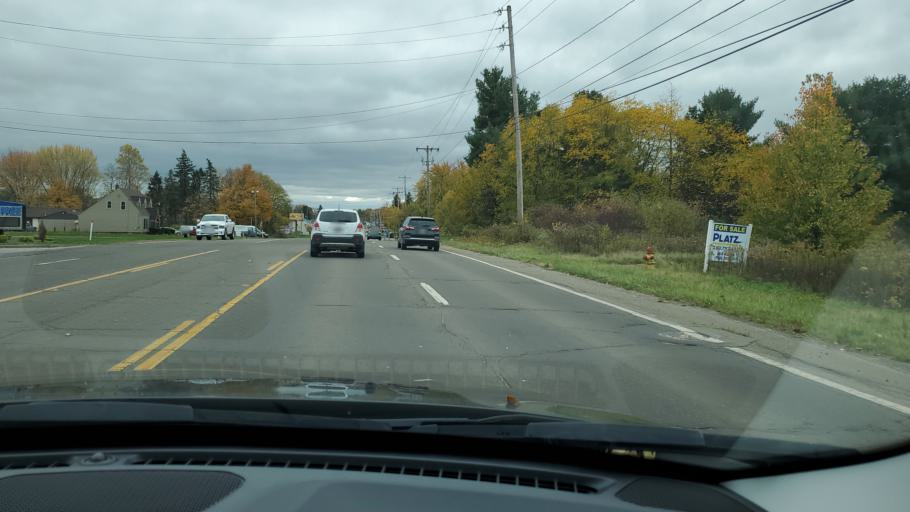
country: US
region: Ohio
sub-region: Mahoning County
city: Boardman
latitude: 40.9921
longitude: -80.6628
